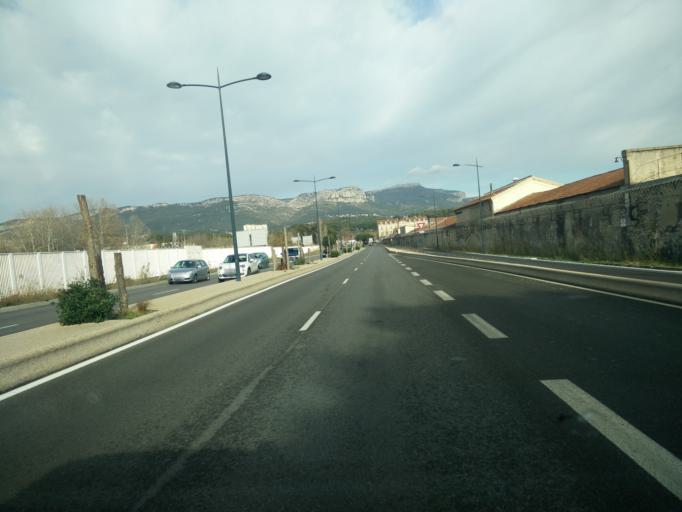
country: FR
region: Provence-Alpes-Cote d'Azur
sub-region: Departement du Var
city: La Seyne-sur-Mer
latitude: 43.1145
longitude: 5.8833
